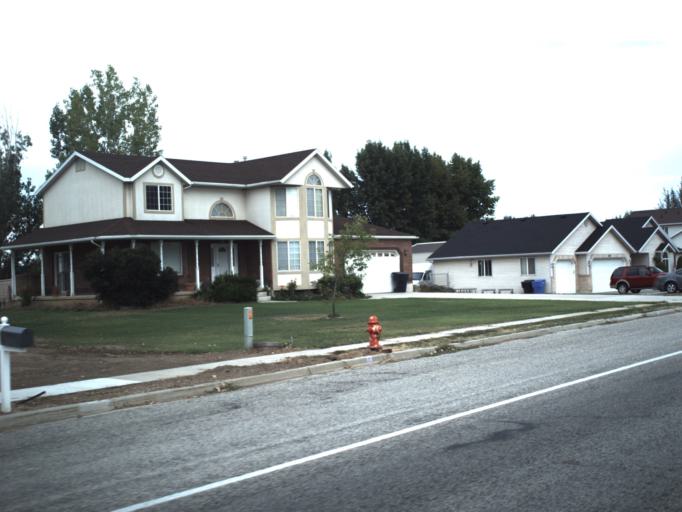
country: US
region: Utah
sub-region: Weber County
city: Plain City
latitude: 41.2823
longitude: -112.0933
